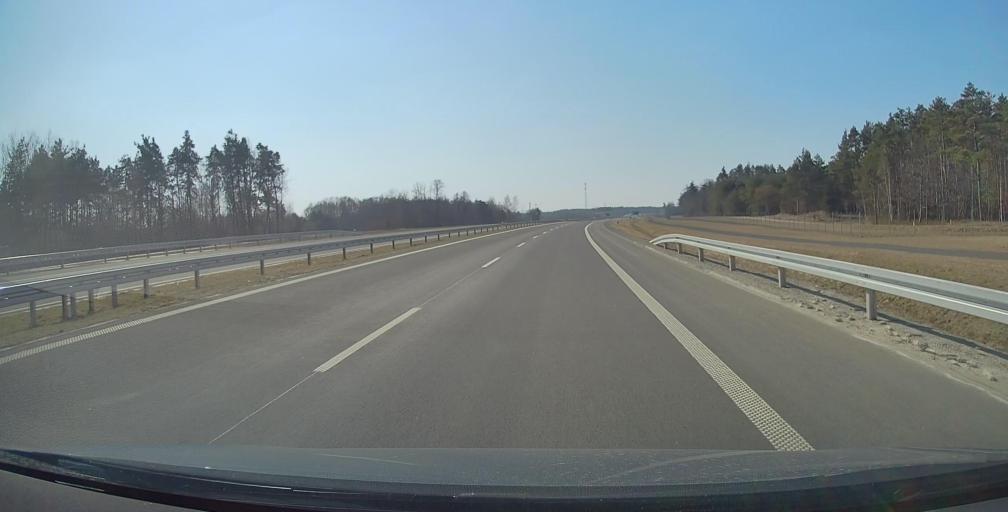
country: PL
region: Lublin Voivodeship
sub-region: Powiat janowski
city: Janow Lubelski
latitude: 50.7066
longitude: 22.3851
